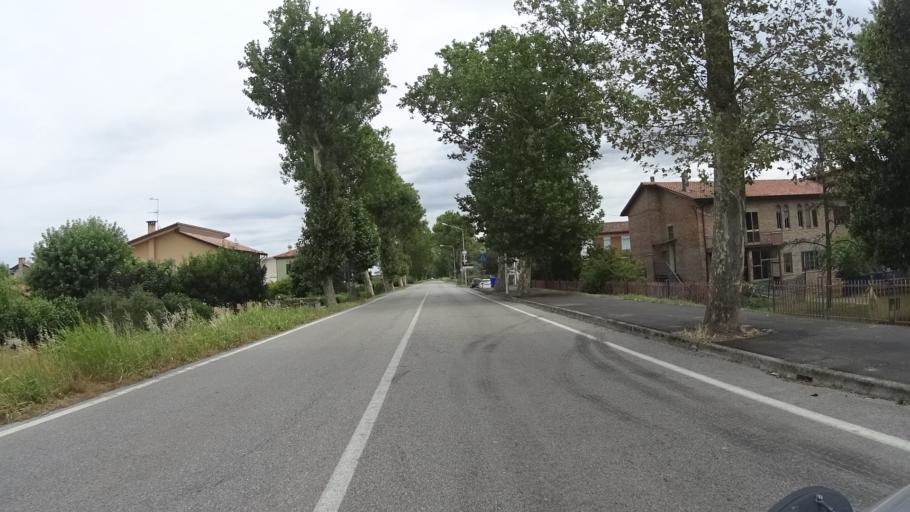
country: IT
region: Veneto
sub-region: Provincia di Venezia
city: Concordia Sagittaria
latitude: 45.7058
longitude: 12.8716
